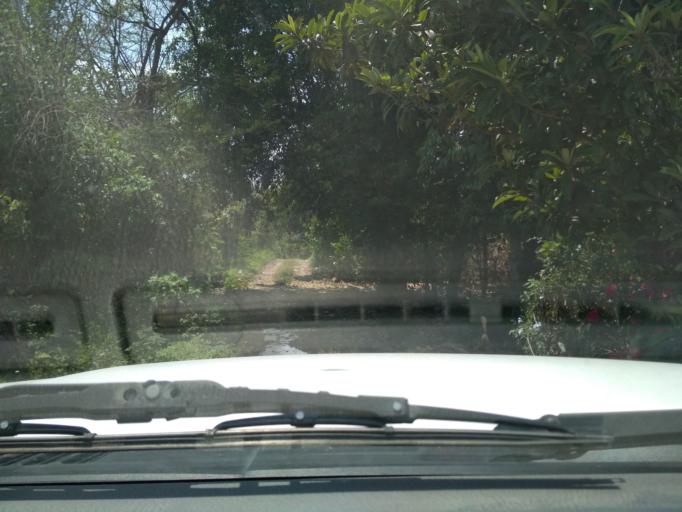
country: MX
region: Veracruz
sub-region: Acultzingo
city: Acatla
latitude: 18.7499
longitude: -97.2230
